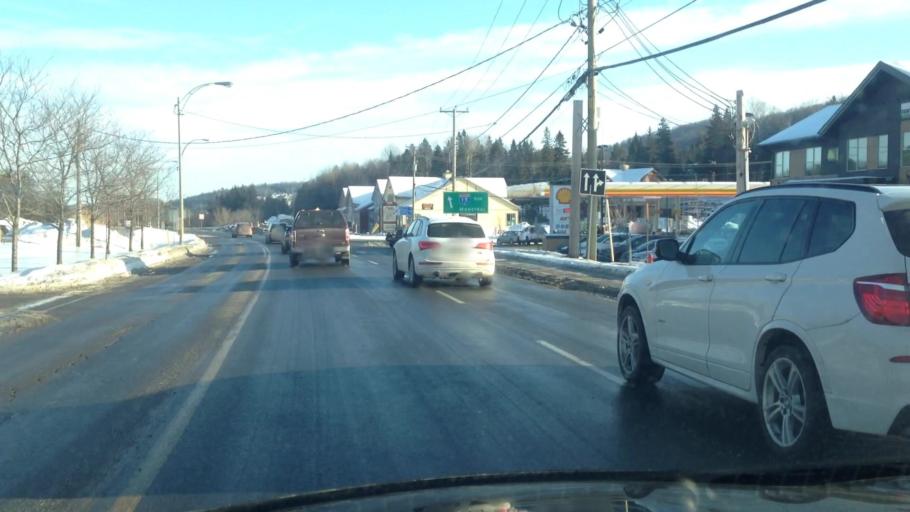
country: CA
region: Quebec
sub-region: Laurentides
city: Saint-Sauveur
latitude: 45.8900
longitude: -74.1467
